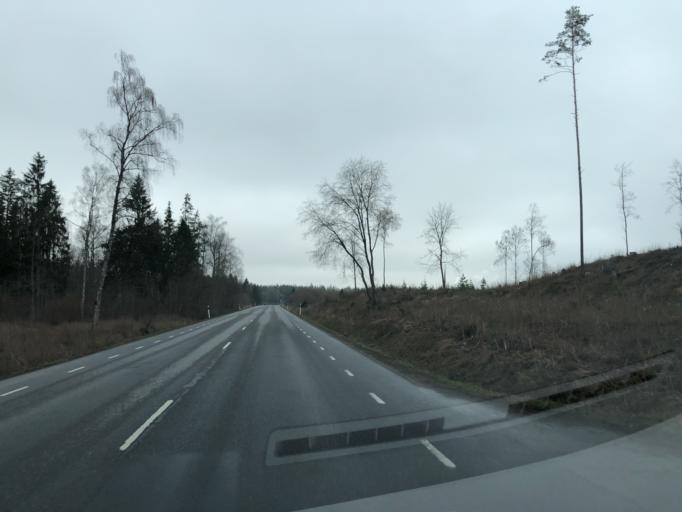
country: EE
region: Laeaene-Virumaa
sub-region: Vaeike-Maarja vald
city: Vaike-Maarja
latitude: 59.0948
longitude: 26.2292
